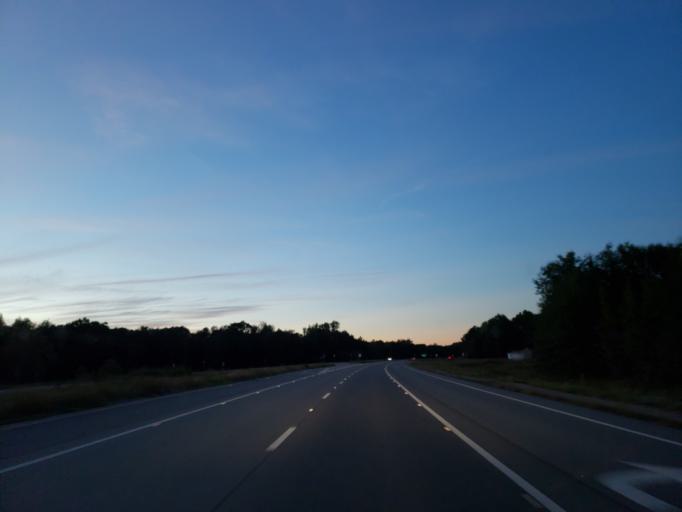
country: US
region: Mississippi
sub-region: Wayne County
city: Waynesboro
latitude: 31.8490
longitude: -88.7163
